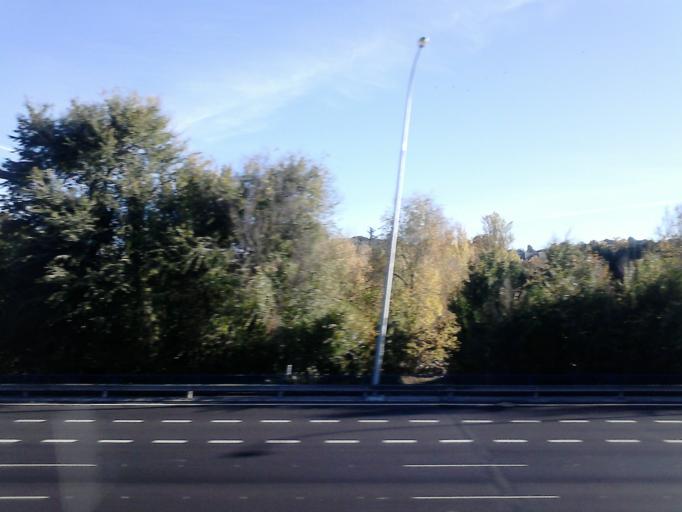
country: ES
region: Madrid
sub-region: Provincia de Madrid
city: Moncloa-Aravaca
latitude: 40.4573
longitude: -3.7466
